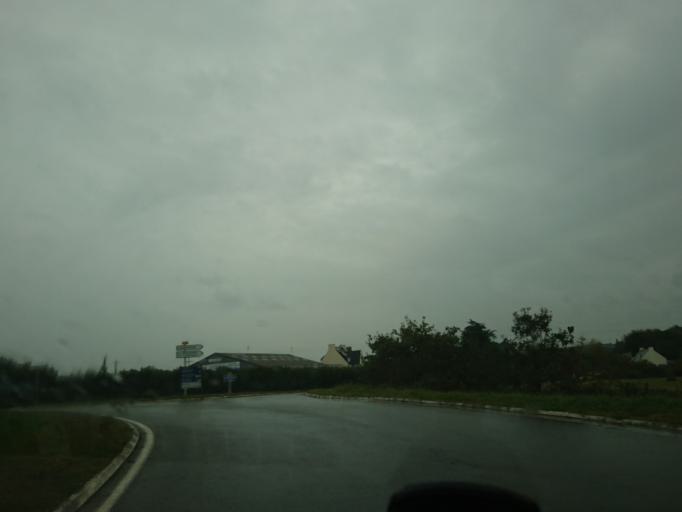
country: FR
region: Brittany
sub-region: Departement du Finistere
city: Plouguerneau
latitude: 48.6031
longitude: -4.5023
